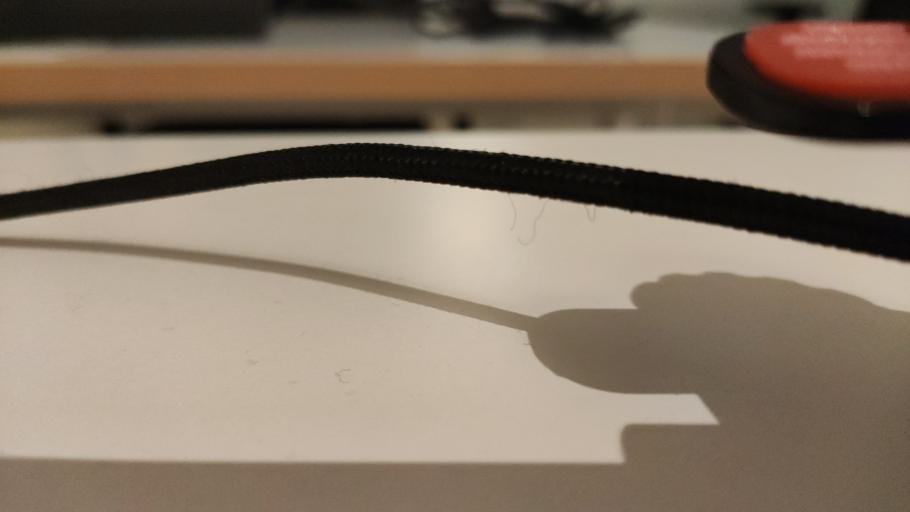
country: RU
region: Moskovskaya
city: Semkhoz
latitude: 56.3965
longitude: 38.0367
